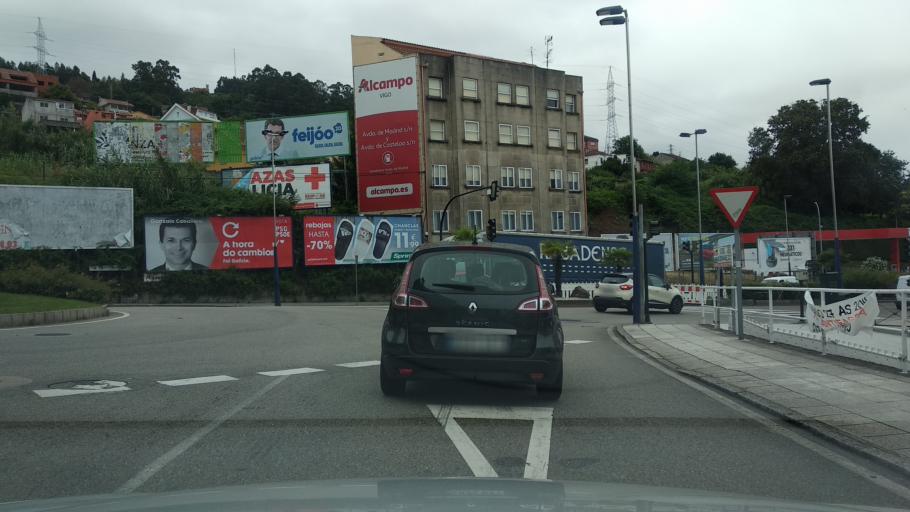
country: ES
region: Galicia
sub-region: Provincia de Pontevedra
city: Vigo
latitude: 42.2469
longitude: -8.6929
